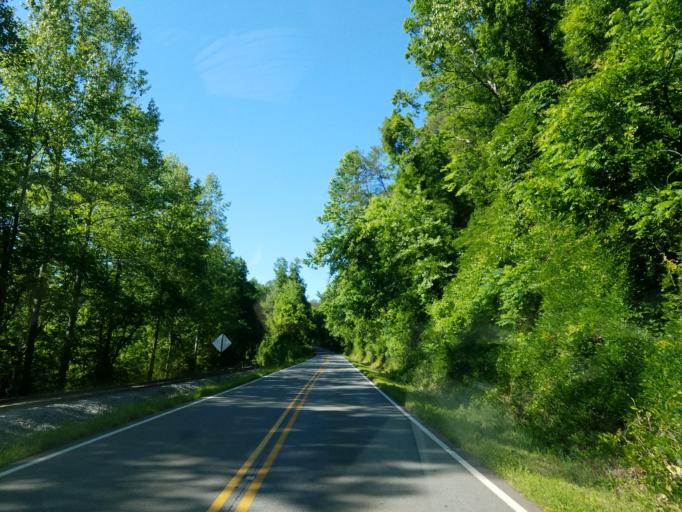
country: US
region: Georgia
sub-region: Pickens County
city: Jasper
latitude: 34.5275
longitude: -84.5089
